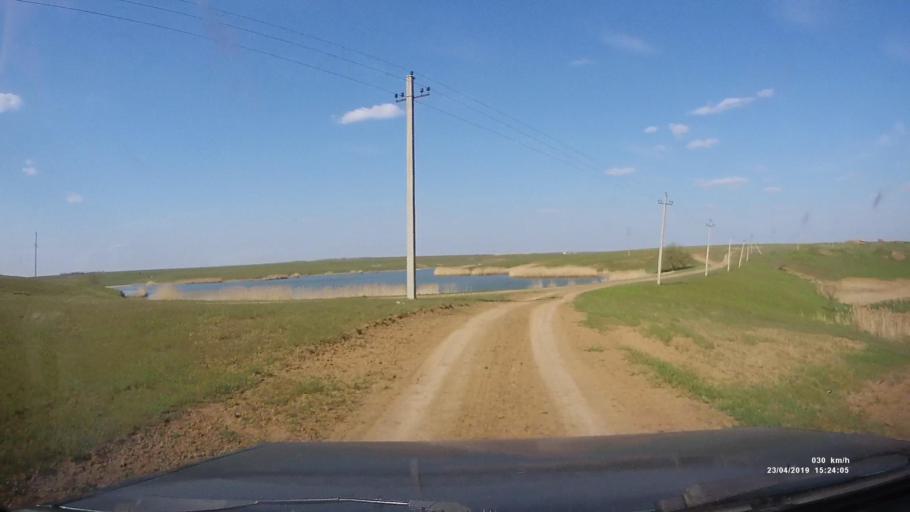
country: RU
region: Rostov
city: Remontnoye
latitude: 46.5390
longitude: 42.9703
